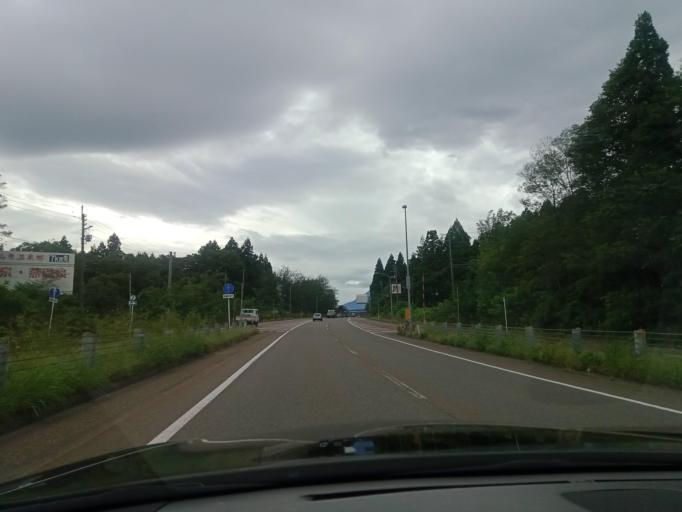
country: JP
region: Niigata
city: Arai
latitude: 36.9653
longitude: 138.2245
